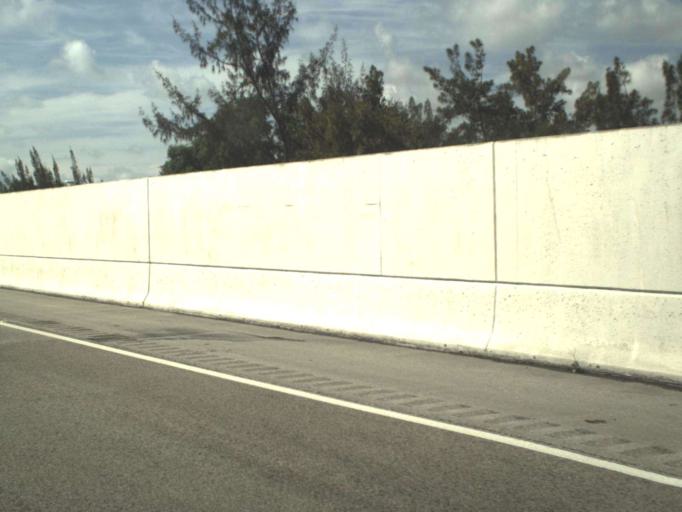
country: US
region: Florida
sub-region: Palm Beach County
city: North Palm Beach
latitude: 26.8451
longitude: -80.1057
